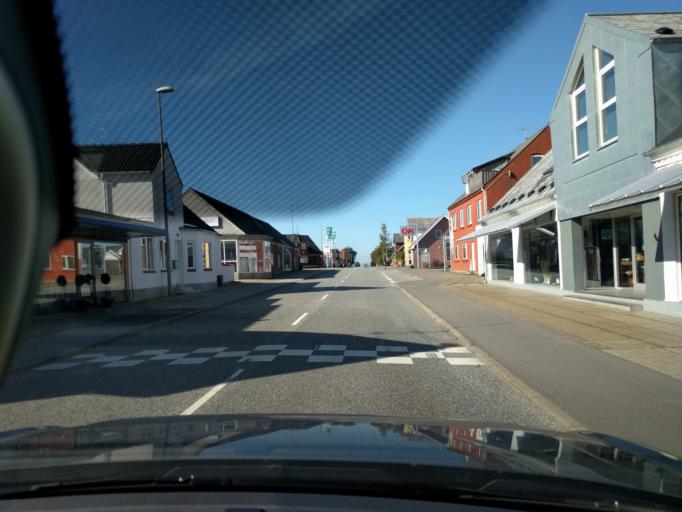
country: DK
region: North Denmark
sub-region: Vesthimmerland Kommune
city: Alestrup
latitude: 56.7073
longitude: 9.6296
